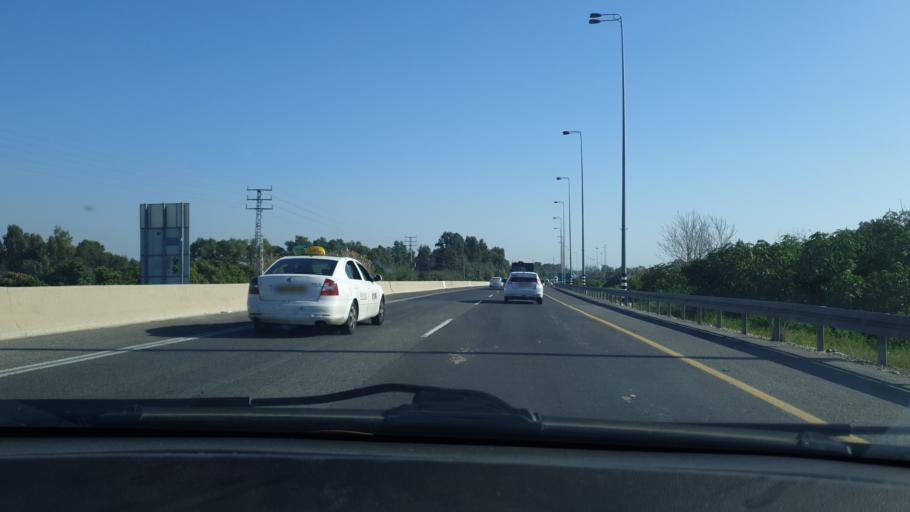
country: IL
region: Central District
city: Kefar Habad
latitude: 31.9581
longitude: 34.8529
